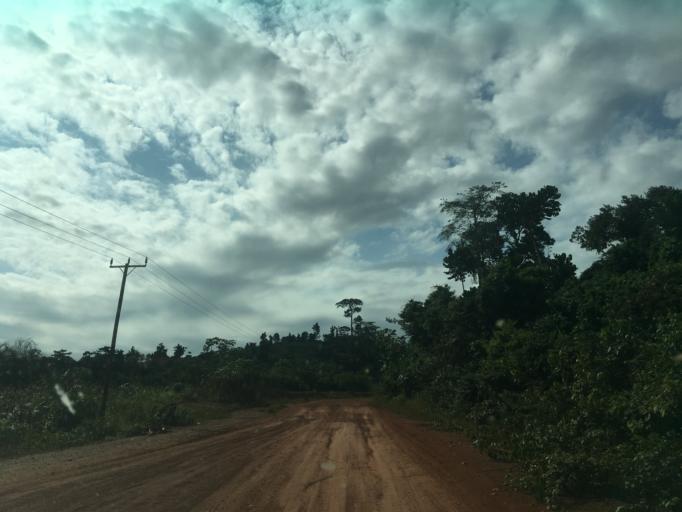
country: GH
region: Western
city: Wassa-Akropong
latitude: 5.9186
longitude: -2.4063
